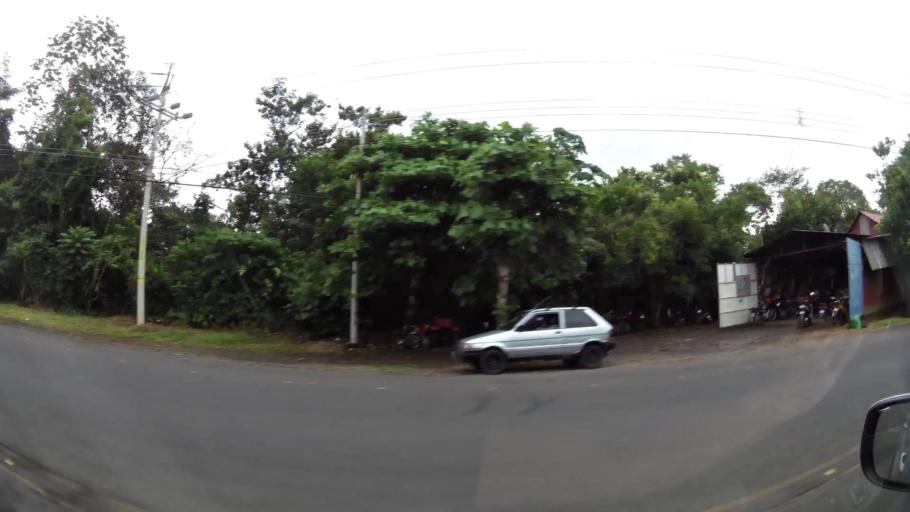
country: CR
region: Alajuela
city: Orotina
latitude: 9.9306
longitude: -84.5204
